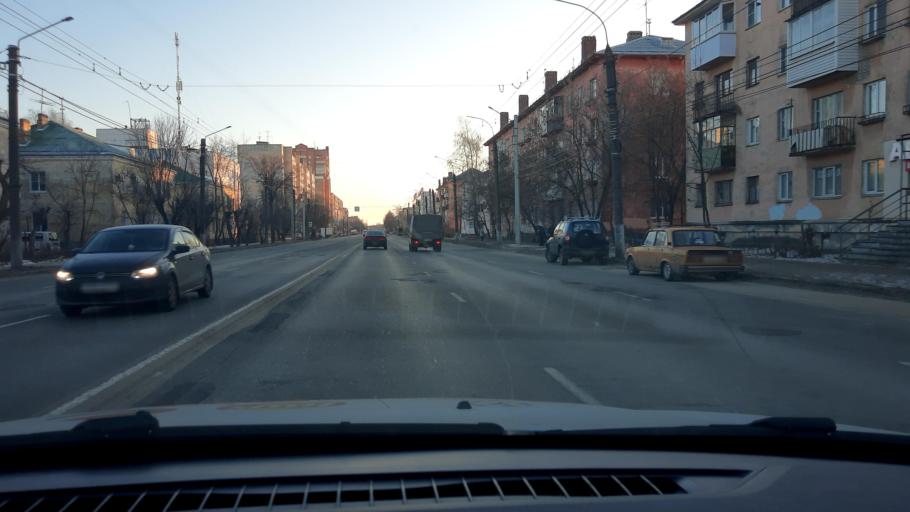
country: RU
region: Nizjnij Novgorod
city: Dzerzhinsk
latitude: 56.2489
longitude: 43.4581
